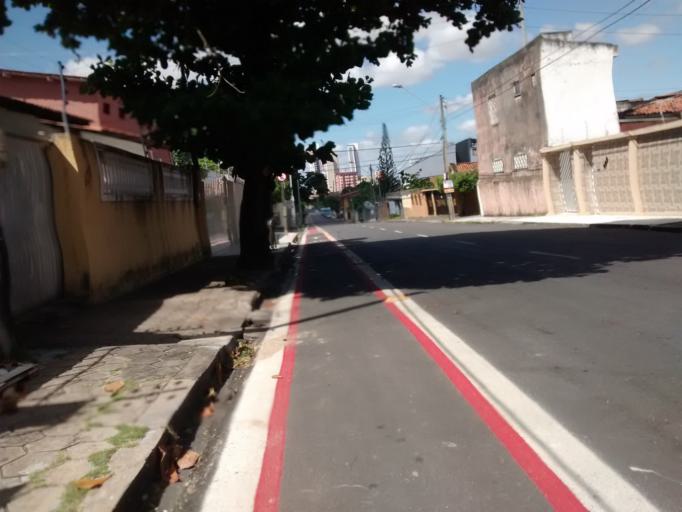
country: BR
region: Ceara
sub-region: Fortaleza
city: Fortaleza
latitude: -3.7276
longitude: -38.5610
